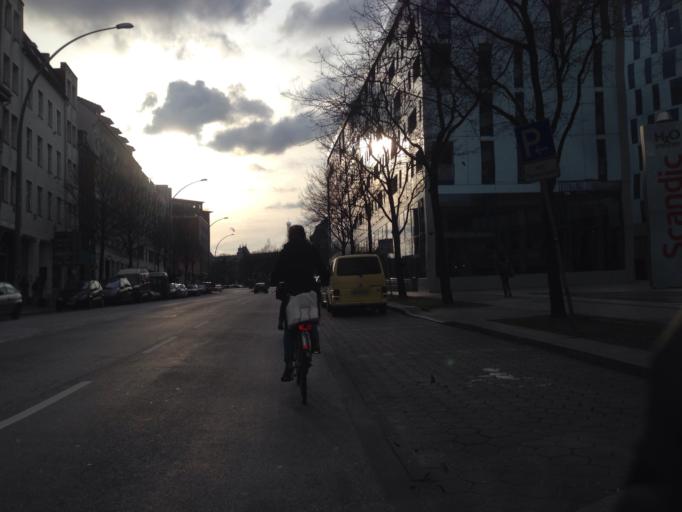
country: DE
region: Hamburg
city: Neustadt
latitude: 53.5557
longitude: 9.9838
